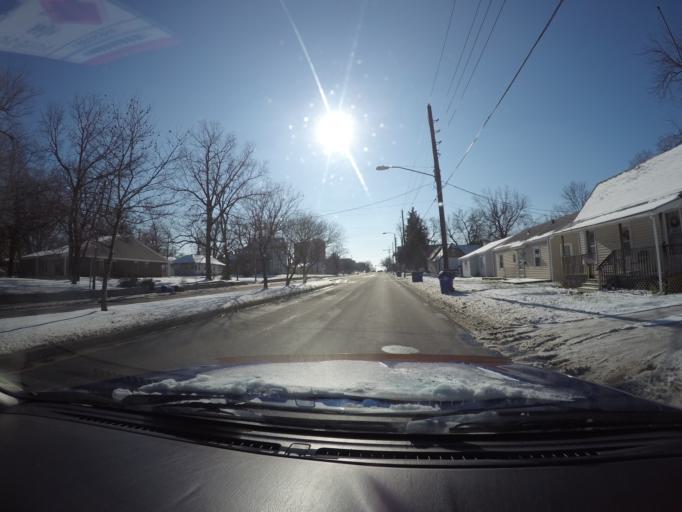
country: US
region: Kansas
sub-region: Johnson County
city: Olathe
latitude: 38.8859
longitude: -94.8207
